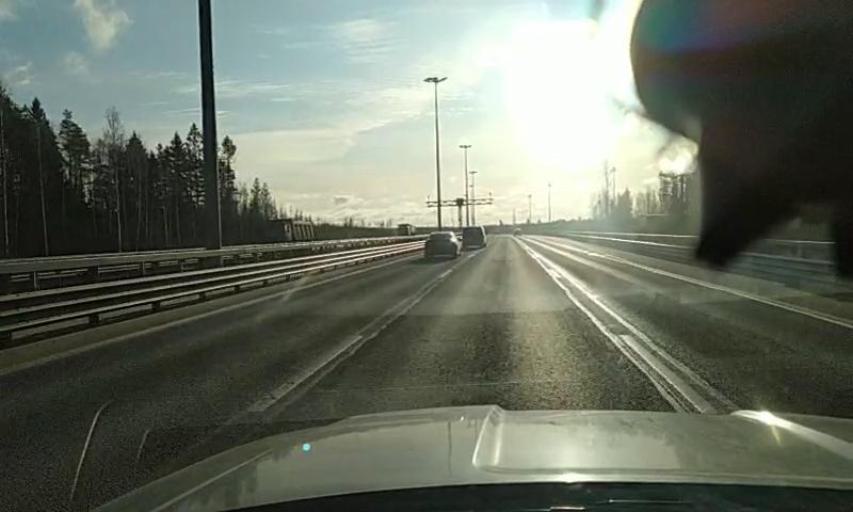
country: RU
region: St.-Petersburg
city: Pesochnyy
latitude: 60.0912
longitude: 30.0980
